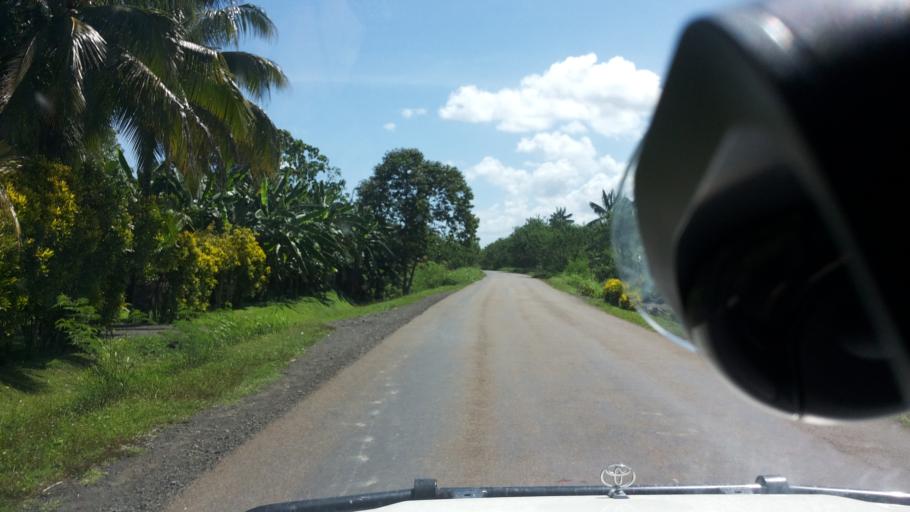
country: PG
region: Madang
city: Madang
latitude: -5.5283
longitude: 145.3788
